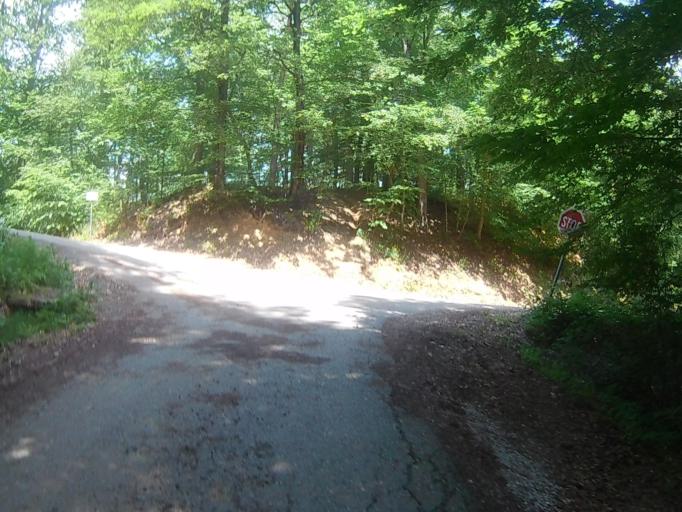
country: SI
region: Kungota
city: Zgornja Kungota
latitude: 46.6245
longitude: 15.6120
